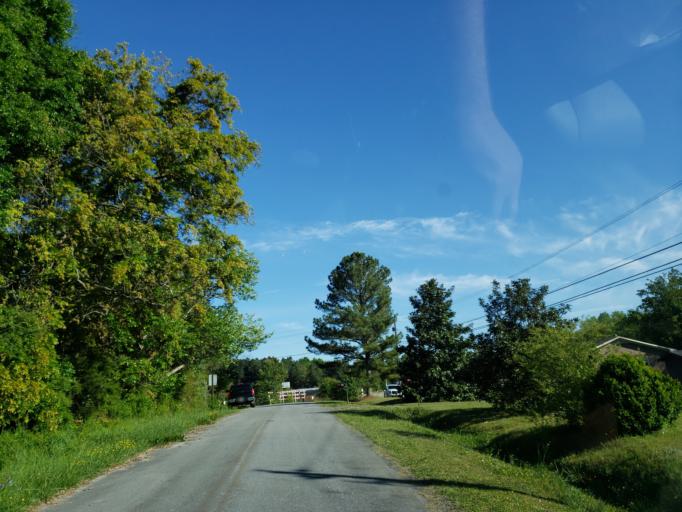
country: US
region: Georgia
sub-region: Polk County
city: Aragon
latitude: 34.0083
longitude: -85.1416
